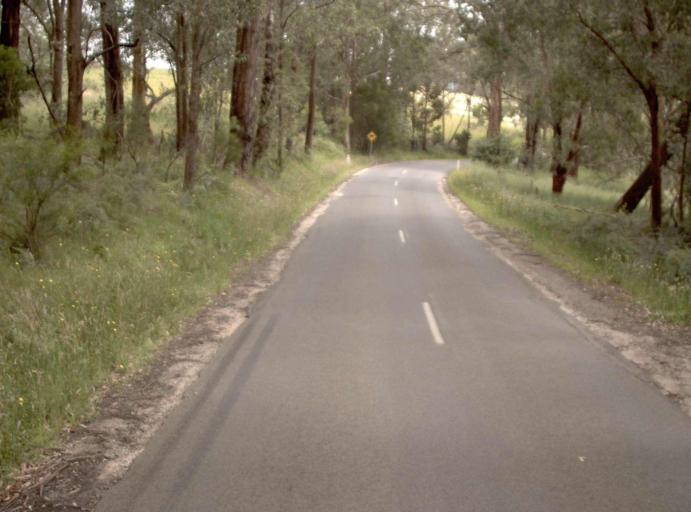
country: AU
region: Victoria
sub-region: Latrobe
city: Moe
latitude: -37.9763
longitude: 146.1384
